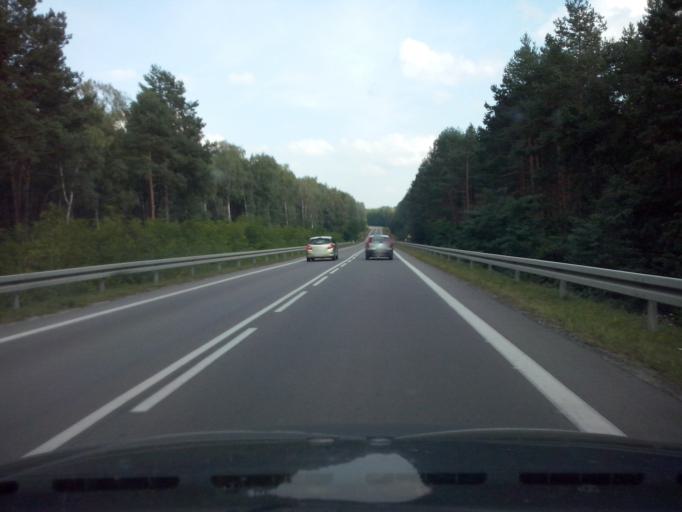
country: PL
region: Subcarpathian Voivodeship
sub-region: Powiat mielecki
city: Przeclaw
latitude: 50.2763
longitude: 21.5378
